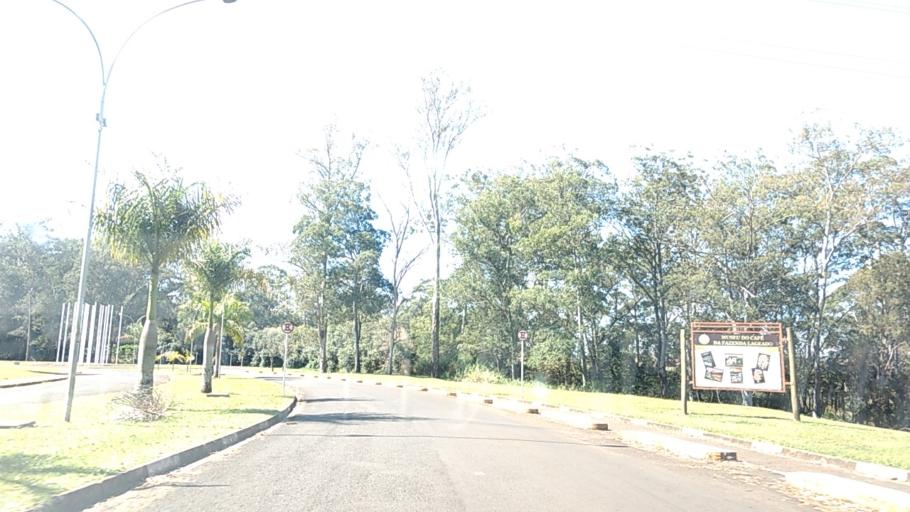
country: BR
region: Sao Paulo
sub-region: Botucatu
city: Botucatu
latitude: -22.8574
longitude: -48.4331
